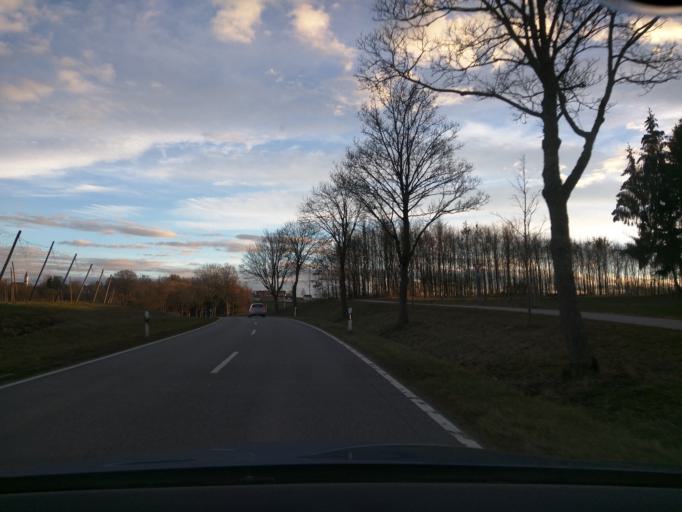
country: DE
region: Bavaria
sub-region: Upper Bavaria
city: Attenkirchen
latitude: 48.5153
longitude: 11.7548
